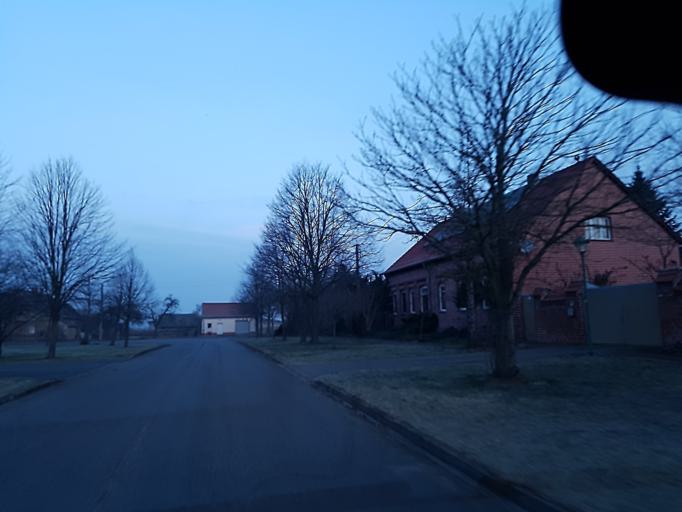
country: DE
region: Brandenburg
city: Herzberg
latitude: 51.7372
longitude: 13.2037
